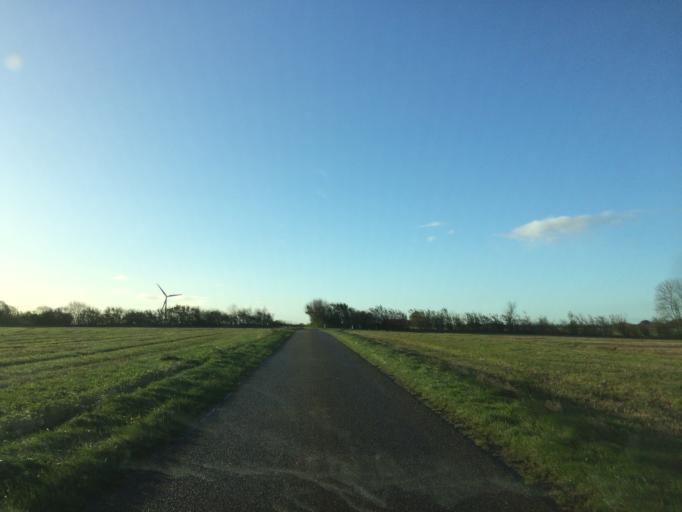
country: DK
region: South Denmark
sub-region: Fredericia Kommune
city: Taulov
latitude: 55.5804
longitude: 9.6579
